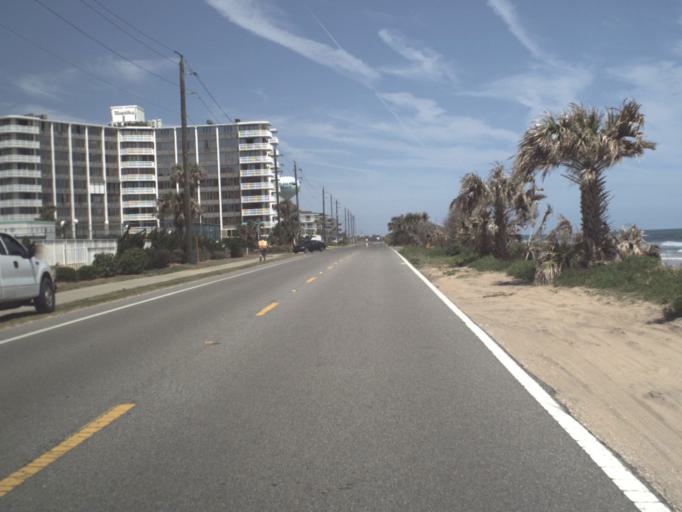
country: US
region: Florida
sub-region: Flagler County
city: Flagler Beach
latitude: 29.4302
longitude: -81.1039
